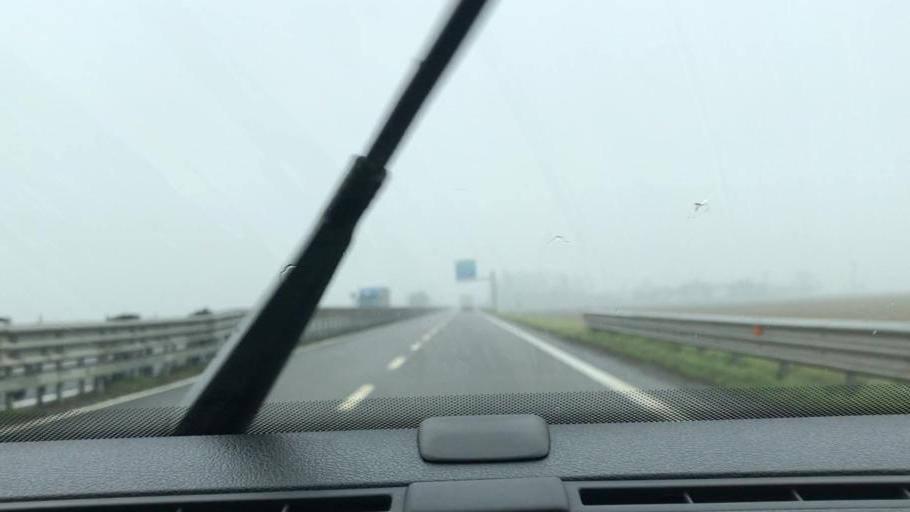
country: IT
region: Veneto
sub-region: Provincia di Rovigo
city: Badia Polesine
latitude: 45.0666
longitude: 11.4970
